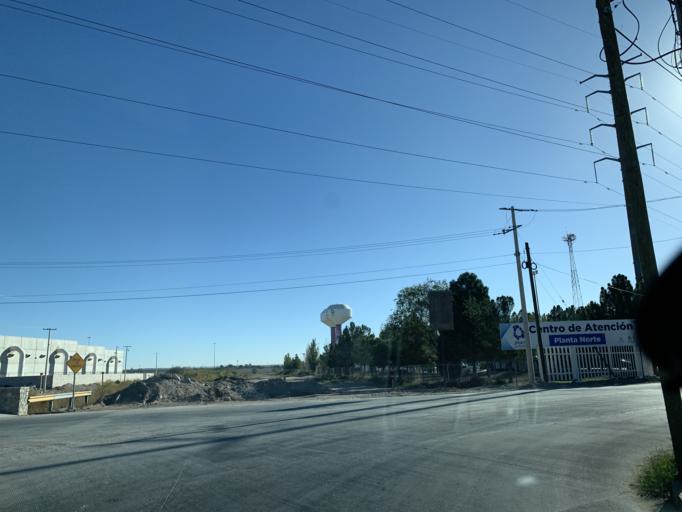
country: US
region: Texas
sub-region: El Paso County
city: Socorro
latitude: 31.7092
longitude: -106.3762
